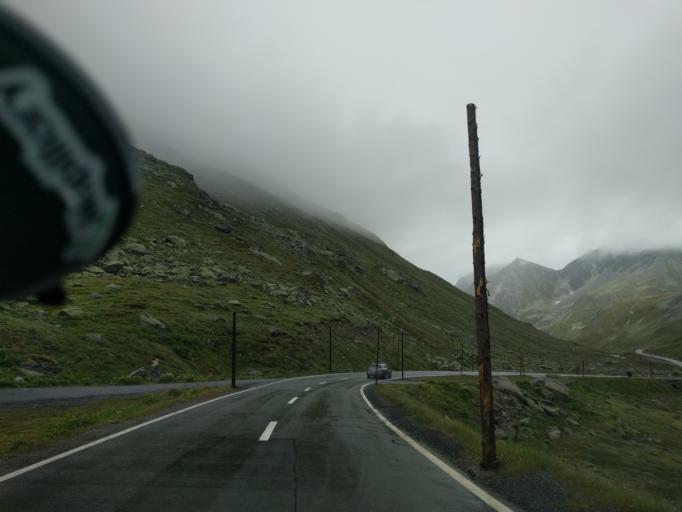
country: CH
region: Grisons
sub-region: Praettigau/Davos District
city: Davos
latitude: 46.7470
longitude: 9.9524
